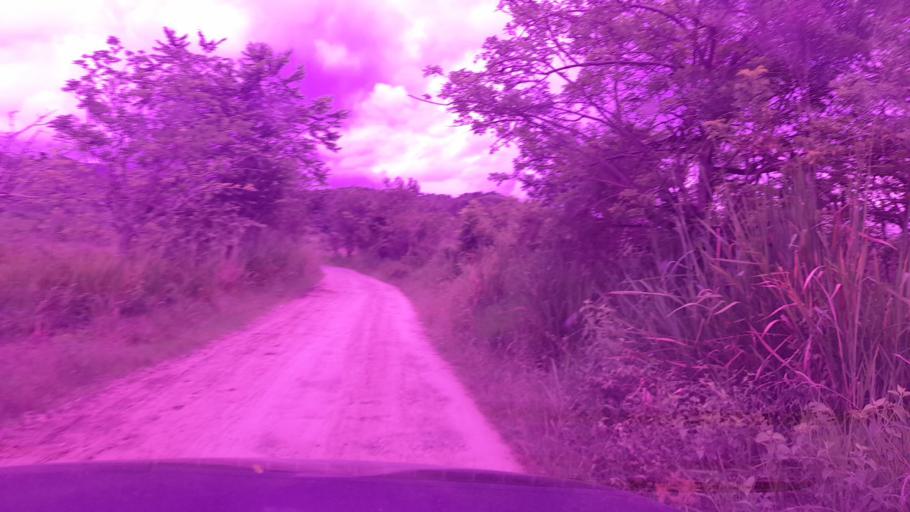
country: CO
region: Valle del Cauca
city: Andalucia
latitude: 4.1765
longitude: -76.1307
